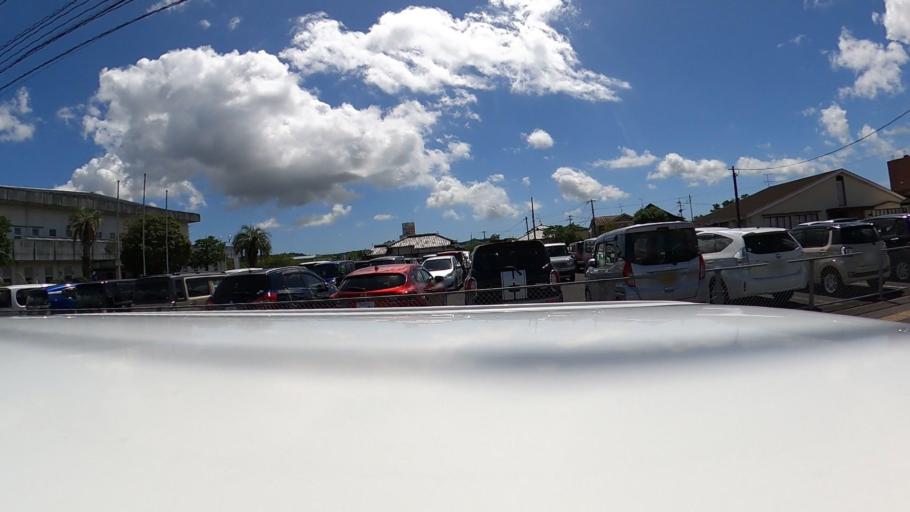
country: JP
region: Miyazaki
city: Tsuma
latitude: 32.1058
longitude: 131.4000
